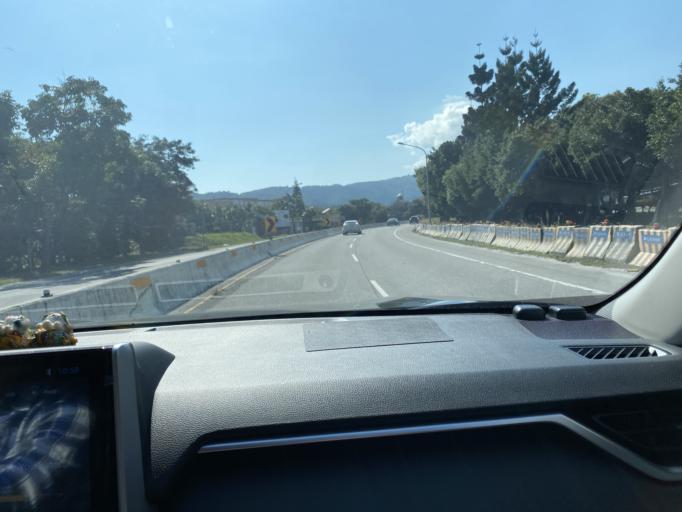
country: TW
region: Taiwan
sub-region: Hualien
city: Hualian
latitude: 23.9326
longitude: 121.5946
